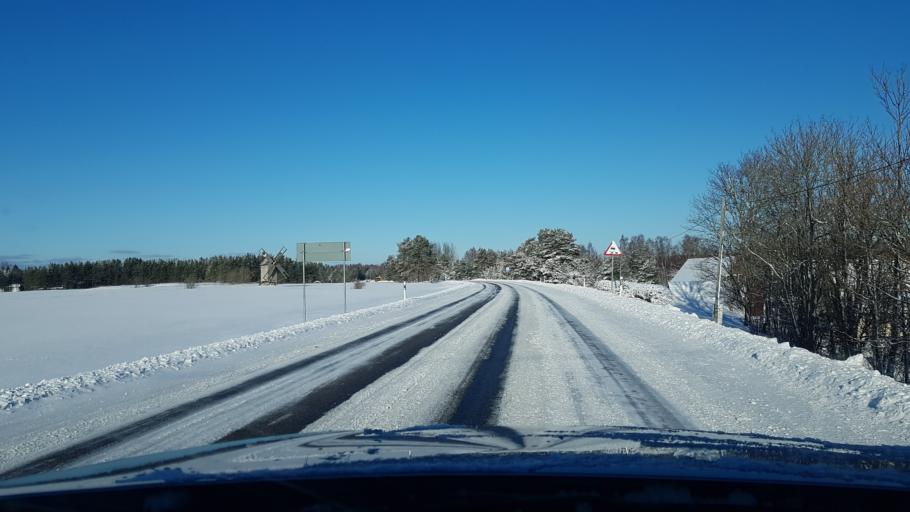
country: EE
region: Hiiumaa
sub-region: Kaerdla linn
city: Kardla
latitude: 58.9561
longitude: 22.7733
